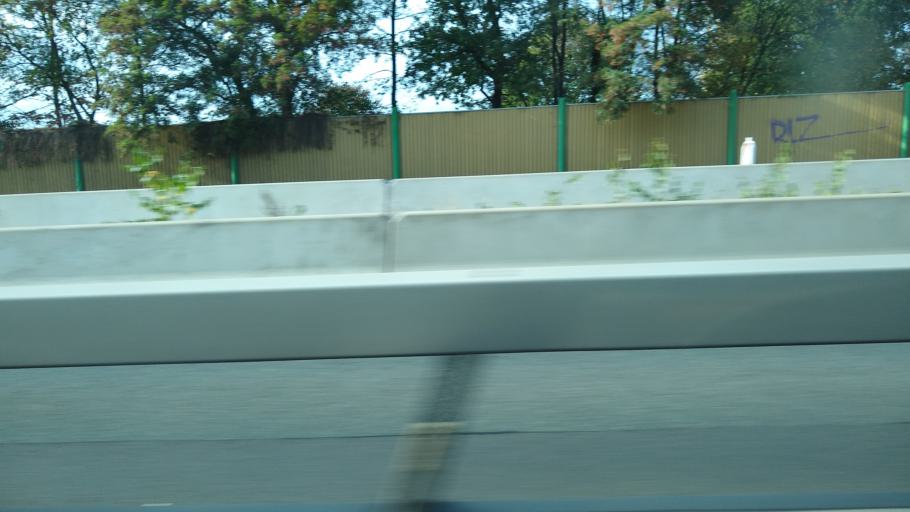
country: DE
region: Lower Saxony
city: Oldenburg
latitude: 53.1679
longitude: 8.2214
